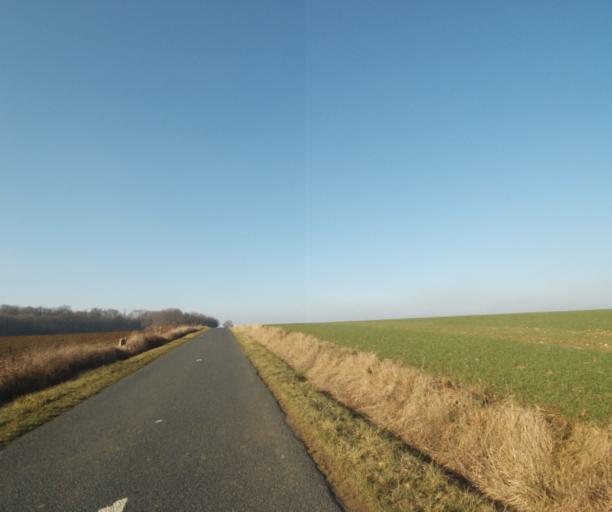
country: FR
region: Champagne-Ardenne
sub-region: Departement de la Haute-Marne
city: Chevillon
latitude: 48.4861
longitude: 5.0836
